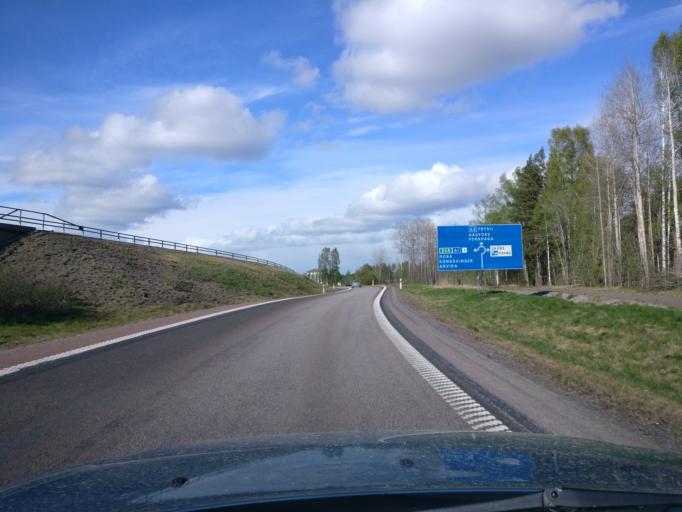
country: SE
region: Vaermland
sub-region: Karlstads Kommun
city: Karlstad
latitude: 59.4271
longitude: 13.4096
